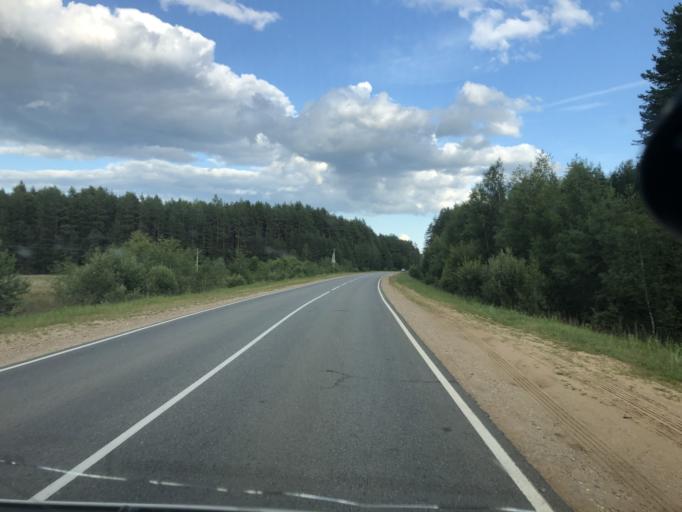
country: RU
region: Kaluga
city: Yukhnov
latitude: 54.7235
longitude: 35.2139
